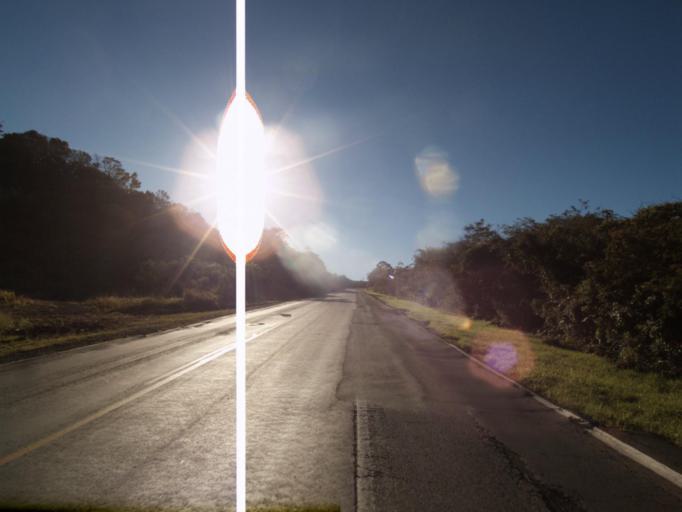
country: AR
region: Misiones
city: Bernardo de Irigoyen
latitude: -26.3248
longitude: -53.5480
